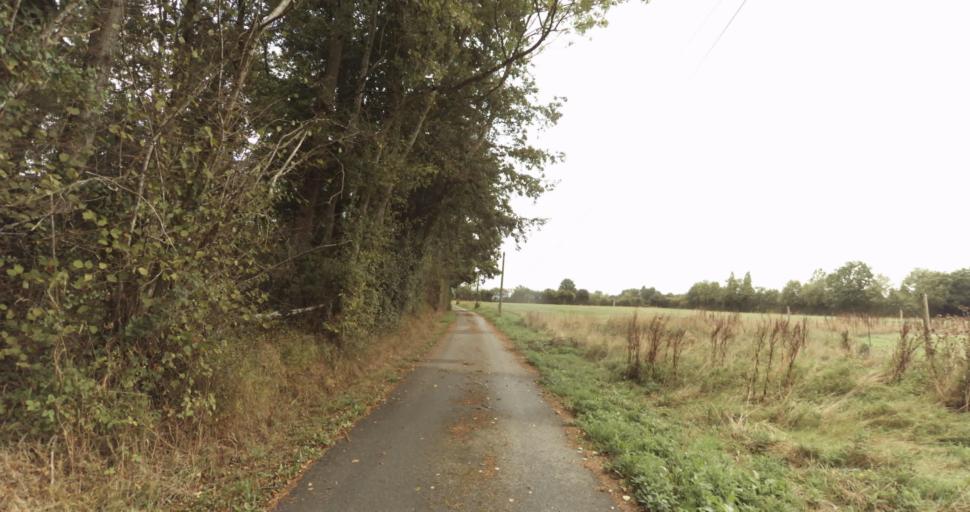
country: FR
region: Lower Normandy
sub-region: Departement de l'Orne
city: Sainte-Gauburge-Sainte-Colombe
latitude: 48.7142
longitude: 0.3842
